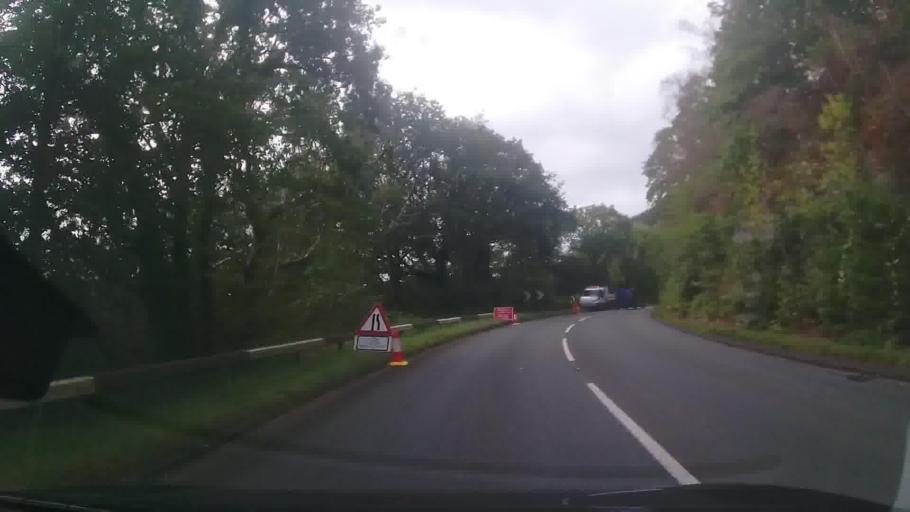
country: GB
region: Wales
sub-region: Gwynedd
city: Dolgellau
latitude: 52.7576
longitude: -3.9202
